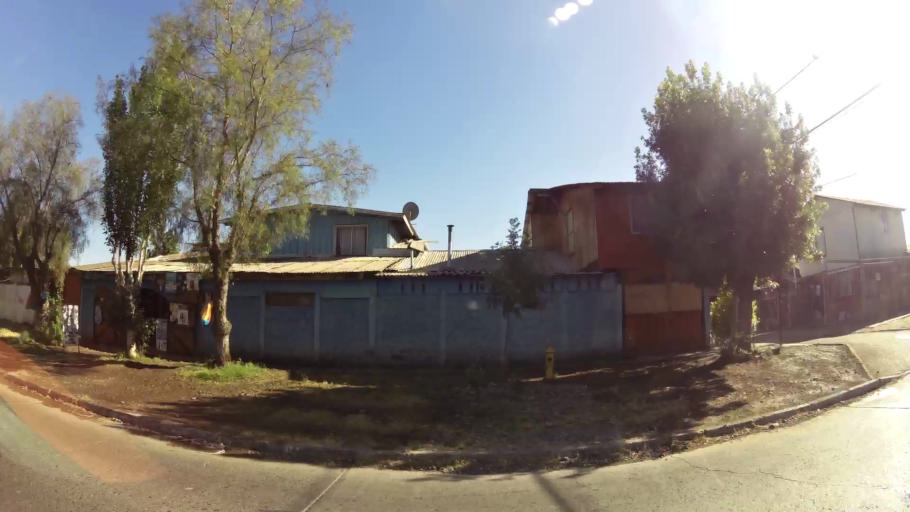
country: CL
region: Santiago Metropolitan
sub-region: Provincia de Maipo
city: San Bernardo
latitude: -33.5523
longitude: -70.6864
